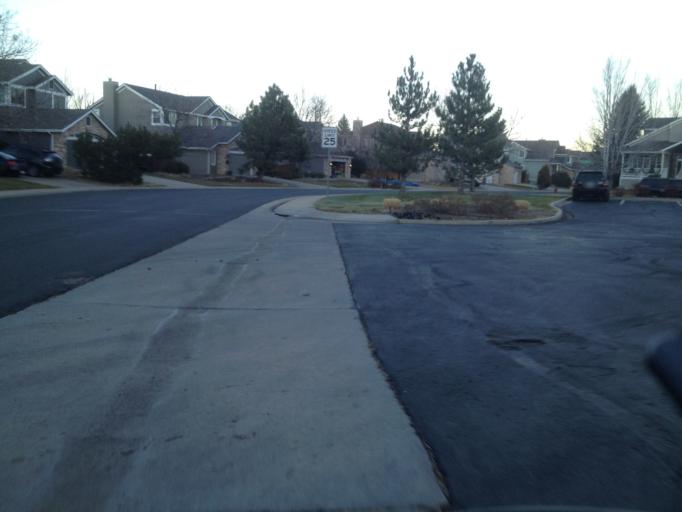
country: US
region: Colorado
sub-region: Boulder County
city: Superior
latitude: 39.9573
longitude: -105.1506
